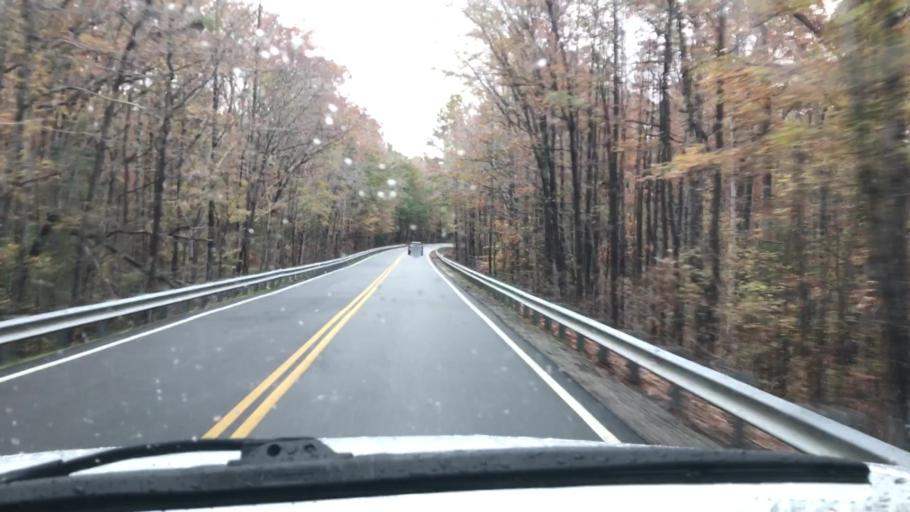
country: US
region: Virginia
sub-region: Henrico County
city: Short Pump
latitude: 37.6049
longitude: -77.6981
